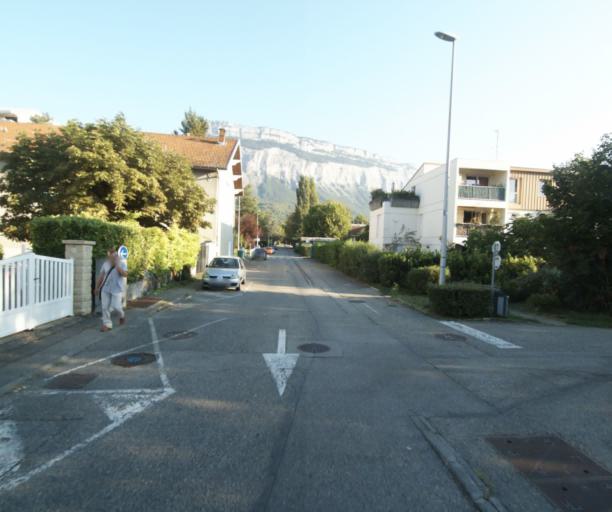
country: FR
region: Rhone-Alpes
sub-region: Departement de l'Isere
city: Corenc
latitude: 45.2077
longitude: 5.7804
